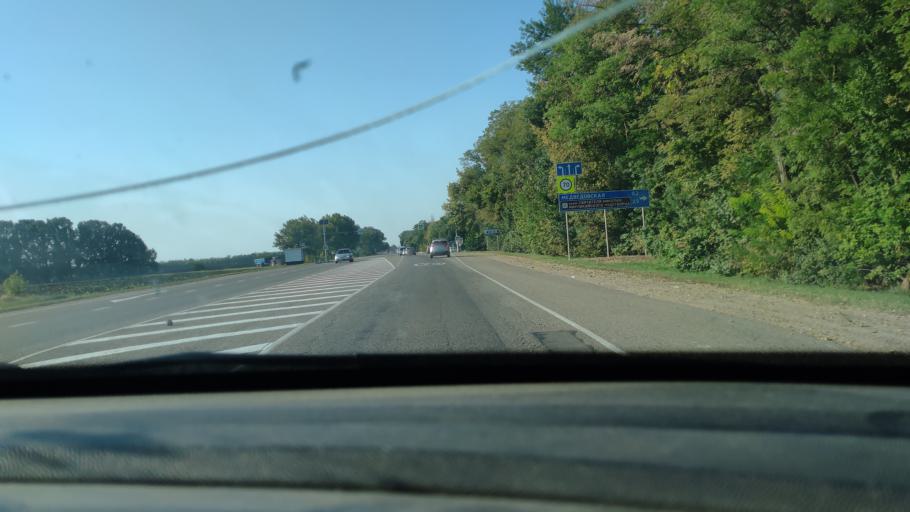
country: RU
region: Krasnodarskiy
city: Medvedovskaya
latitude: 45.4513
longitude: 38.9912
